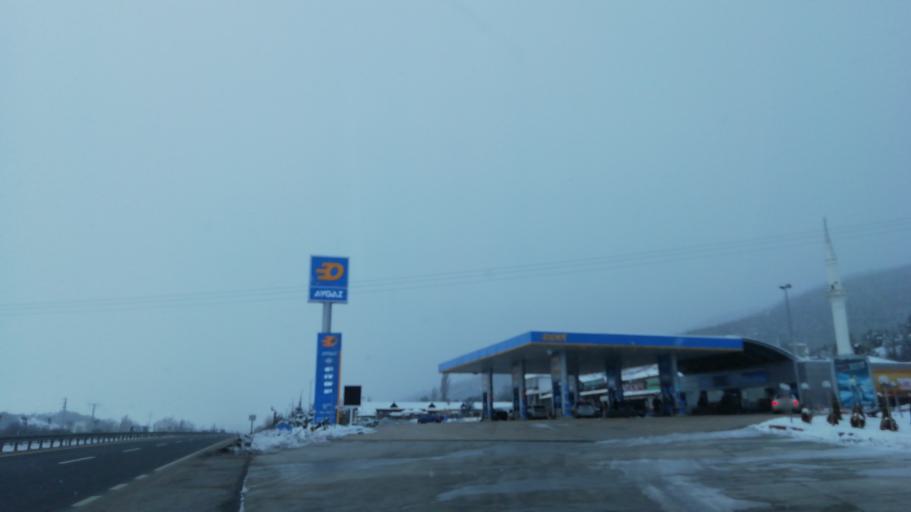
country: TR
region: Bolu
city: Gerede
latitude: 40.8178
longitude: 32.2954
